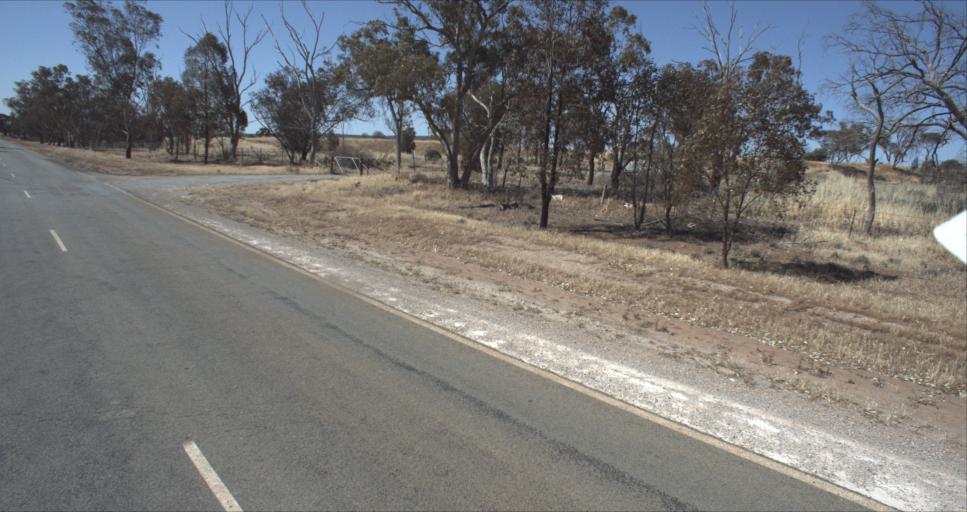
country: AU
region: New South Wales
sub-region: Leeton
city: Leeton
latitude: -34.5000
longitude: 146.4337
